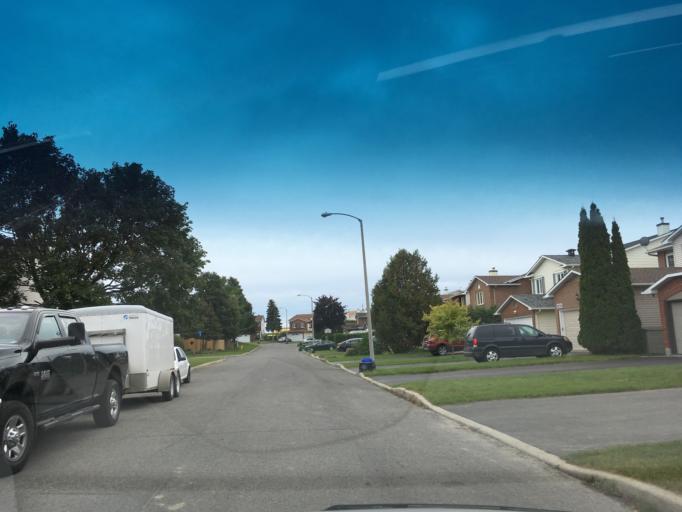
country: CA
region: Quebec
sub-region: Outaouais
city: Gatineau
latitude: 45.4578
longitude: -75.5051
